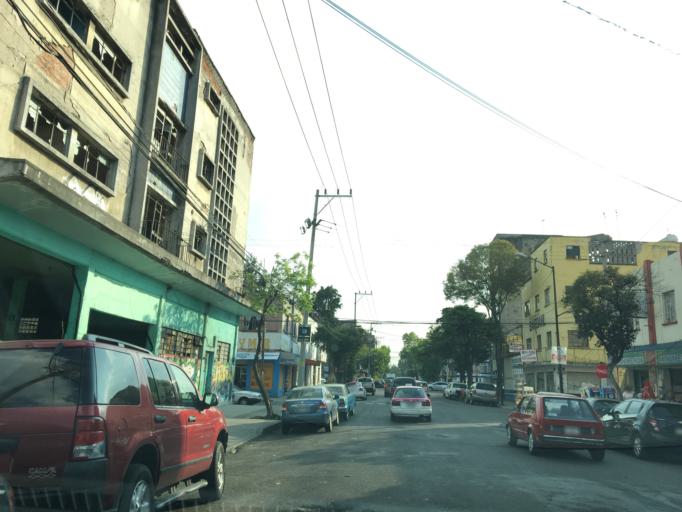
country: MX
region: Mexico City
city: Mexico City
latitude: 19.4162
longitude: -99.1364
